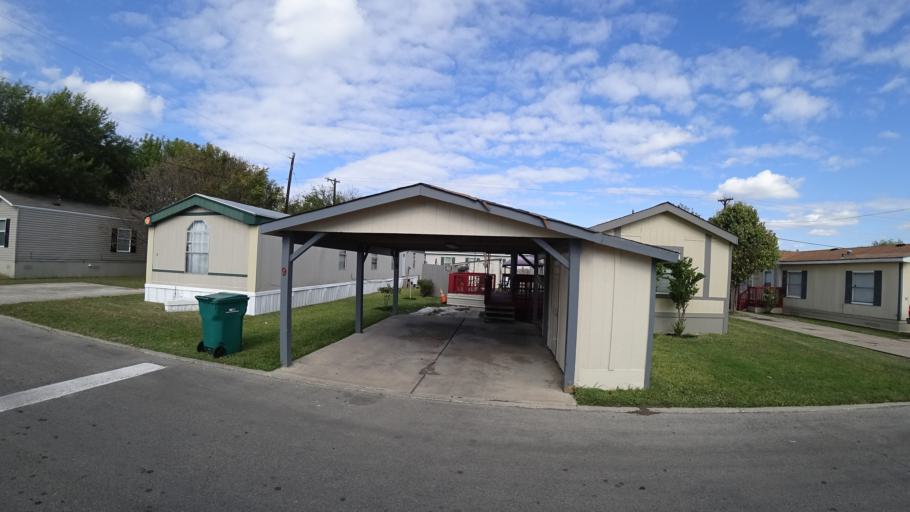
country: US
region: Texas
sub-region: Travis County
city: Pflugerville
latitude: 30.4347
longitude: -97.6397
